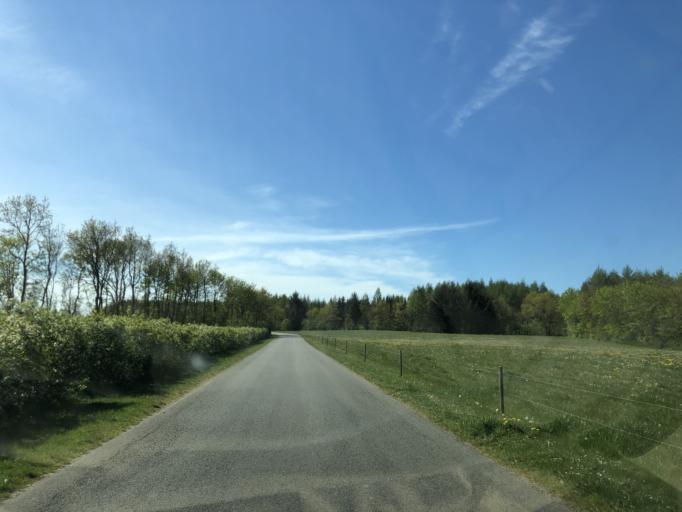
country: DK
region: Central Jutland
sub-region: Ringkobing-Skjern Kommune
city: Videbaek
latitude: 56.1906
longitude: 8.5159
